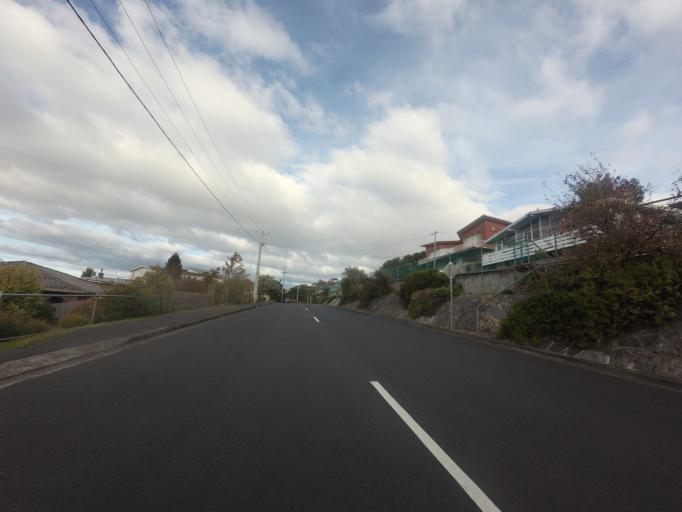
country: AU
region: Tasmania
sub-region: Glenorchy
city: Berriedale
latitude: -42.8170
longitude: 147.2414
